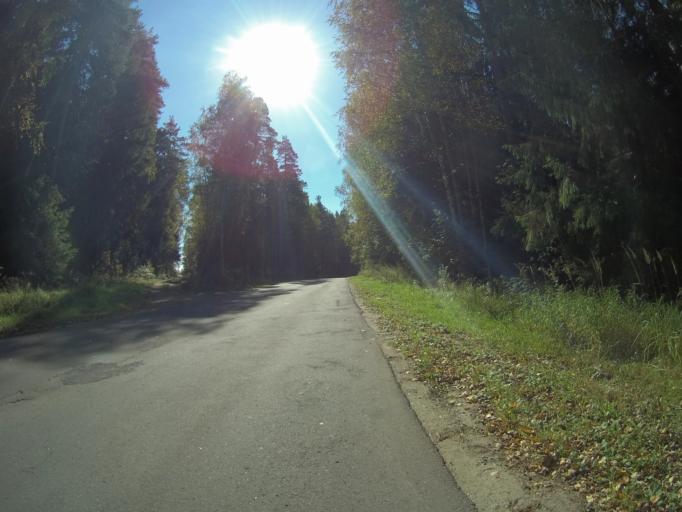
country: RU
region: Vladimir
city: Raduzhnyy
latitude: 55.9532
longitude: 40.2502
